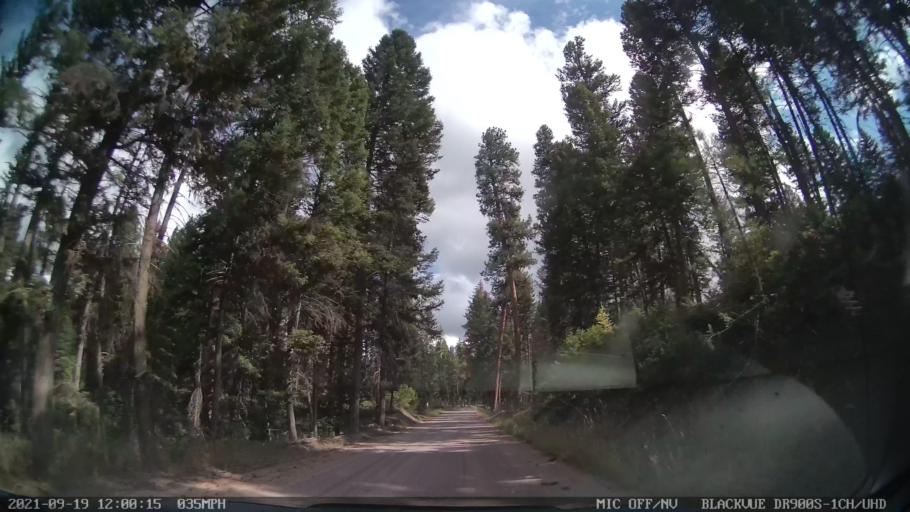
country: US
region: Montana
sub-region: Missoula County
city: Seeley Lake
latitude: 47.1878
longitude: -113.4680
